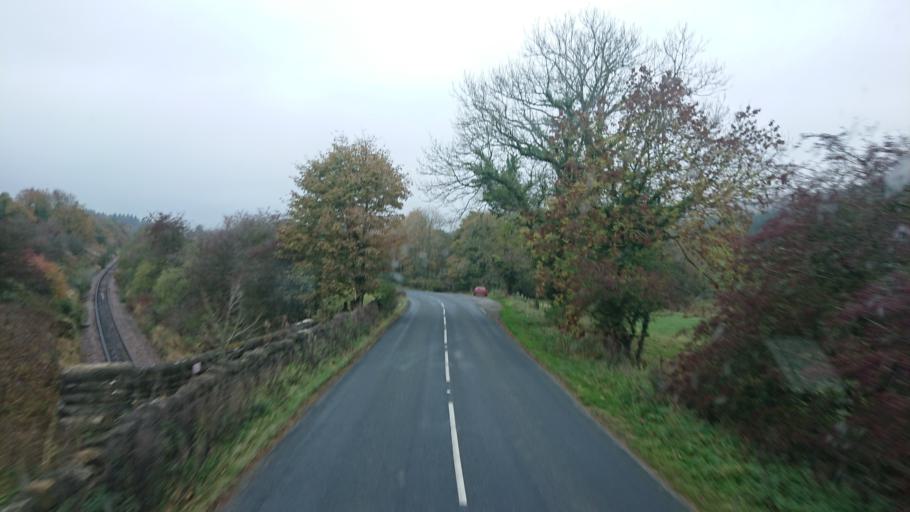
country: GB
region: England
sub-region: North Yorkshire
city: Skipton
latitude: 53.9960
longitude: -2.0406
